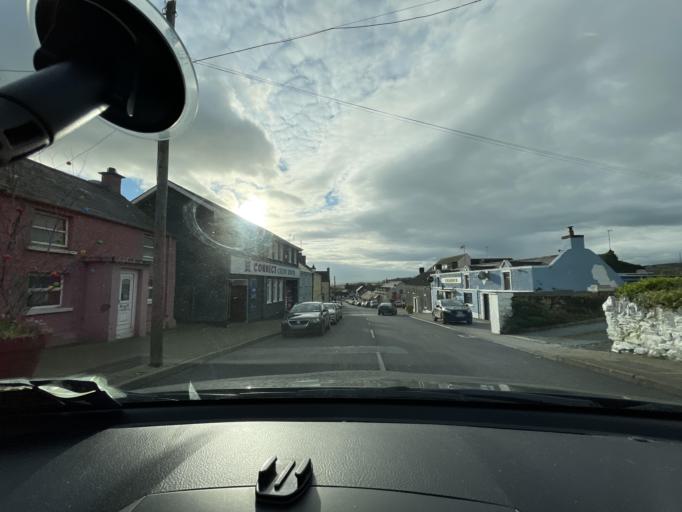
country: IE
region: Leinster
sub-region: Lu
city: Clogherhead
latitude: 53.7925
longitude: -6.2386
